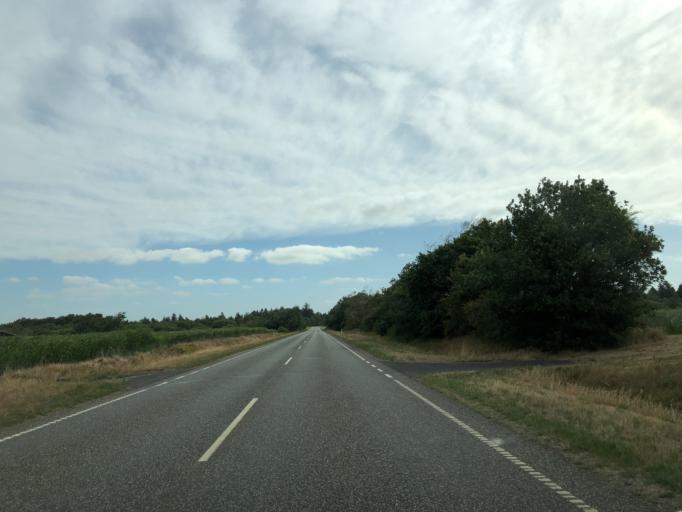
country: DK
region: Central Jutland
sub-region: Herning Kommune
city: Sunds
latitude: 56.3238
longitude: 8.9354
